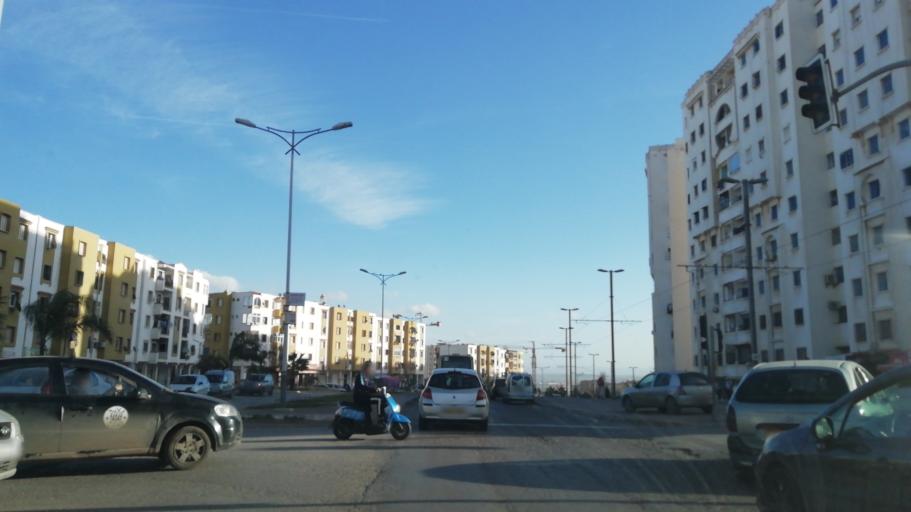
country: DZ
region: Oran
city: Bir el Djir
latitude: 35.7031
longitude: -0.5696
